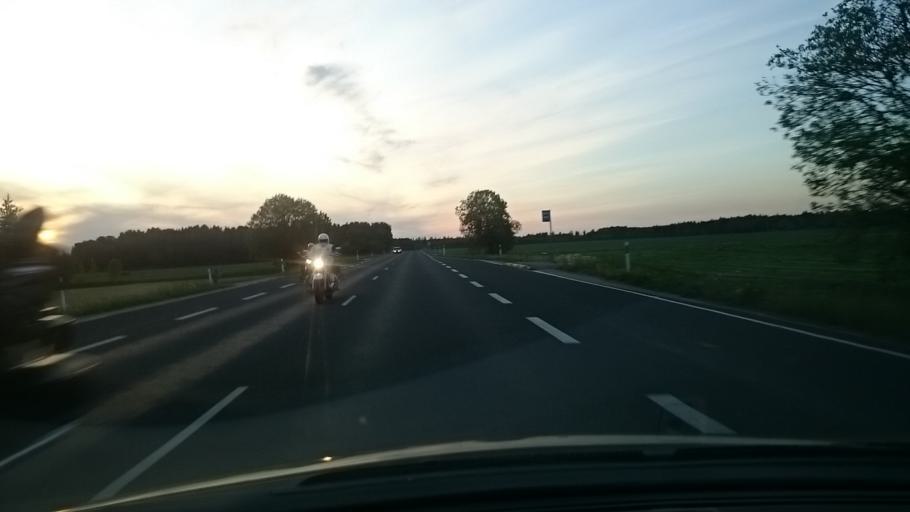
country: EE
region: Viljandimaa
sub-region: Vohma linn
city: Vohma
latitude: 58.7052
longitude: 25.6211
